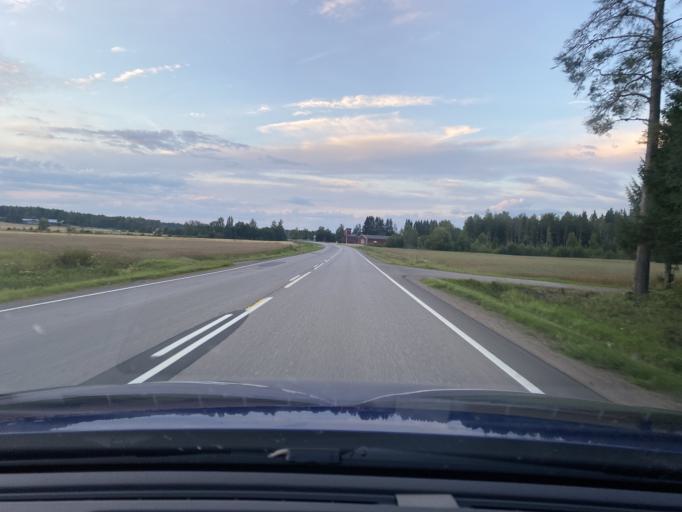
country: FI
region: Satakunta
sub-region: Pohjois-Satakunta
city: Honkajoki
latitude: 61.9820
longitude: 22.2366
